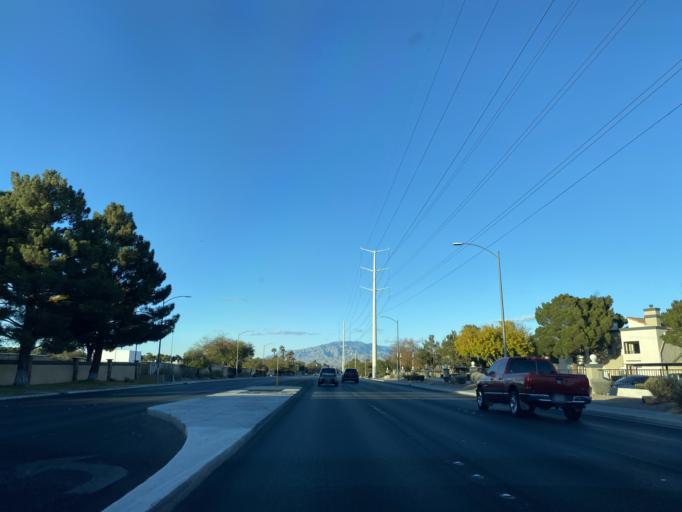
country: US
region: Nevada
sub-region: Clark County
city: Spring Valley
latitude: 36.2001
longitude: -115.2605
